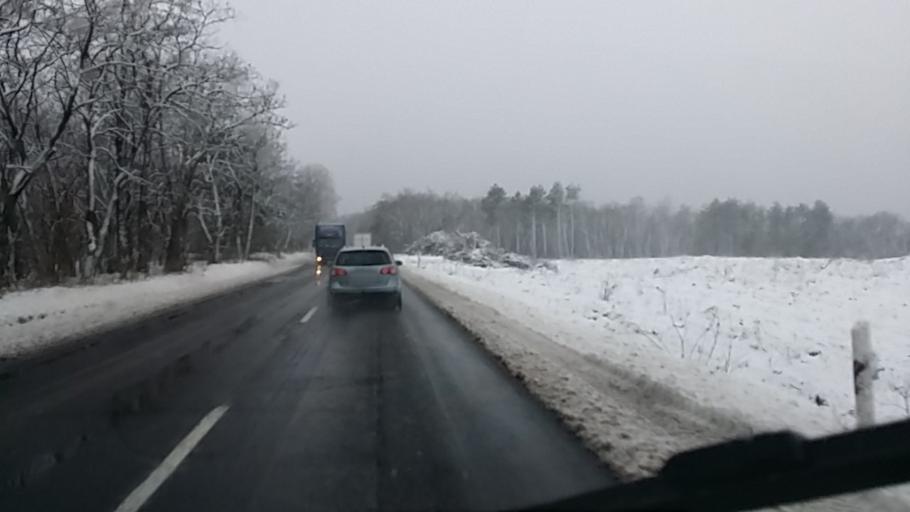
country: HU
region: Komarom-Esztergom
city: Acs
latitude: 47.7395
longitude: 17.9419
